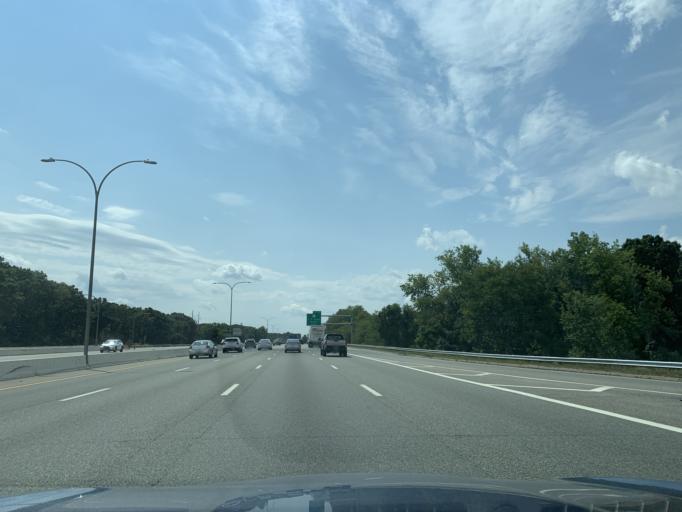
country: US
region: Rhode Island
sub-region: Providence County
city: Cranston
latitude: 41.7455
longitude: -71.4443
